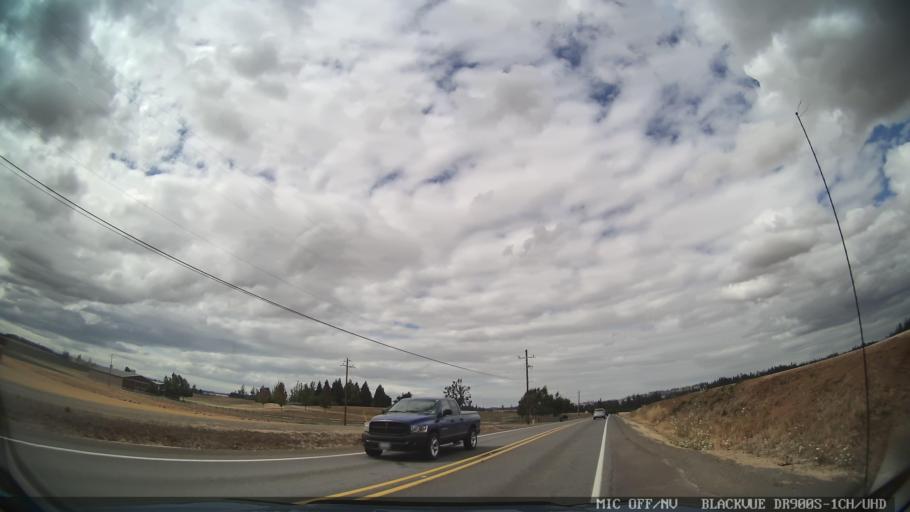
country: US
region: Oregon
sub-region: Marion County
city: Sublimity
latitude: 44.8407
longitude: -122.7946
